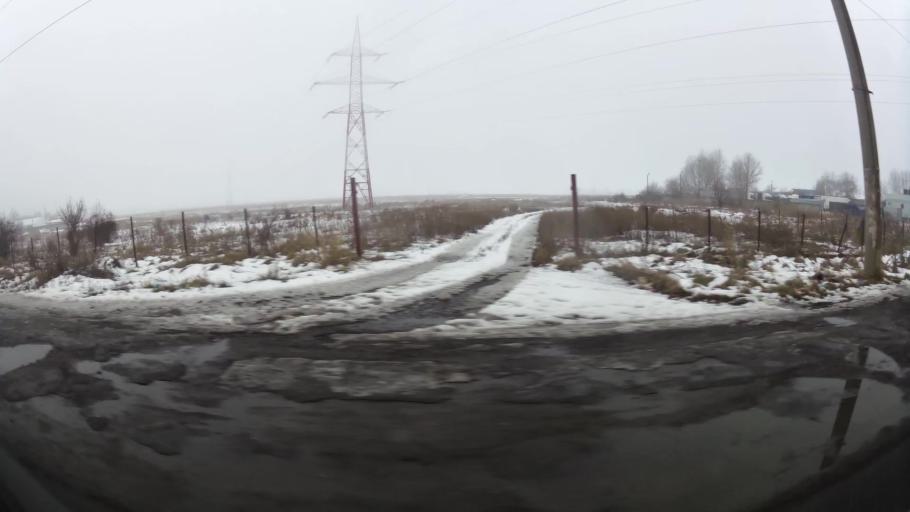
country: RO
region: Ilfov
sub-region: Comuna Clinceni
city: Olteni
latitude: 44.4125
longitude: 25.9726
